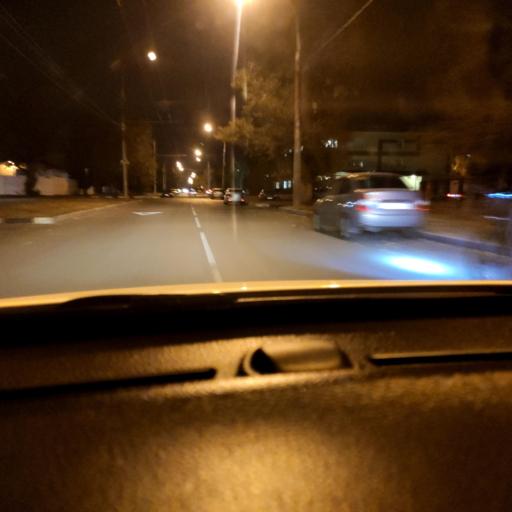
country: RU
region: Voronezj
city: Voronezh
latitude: 51.6379
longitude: 39.2434
